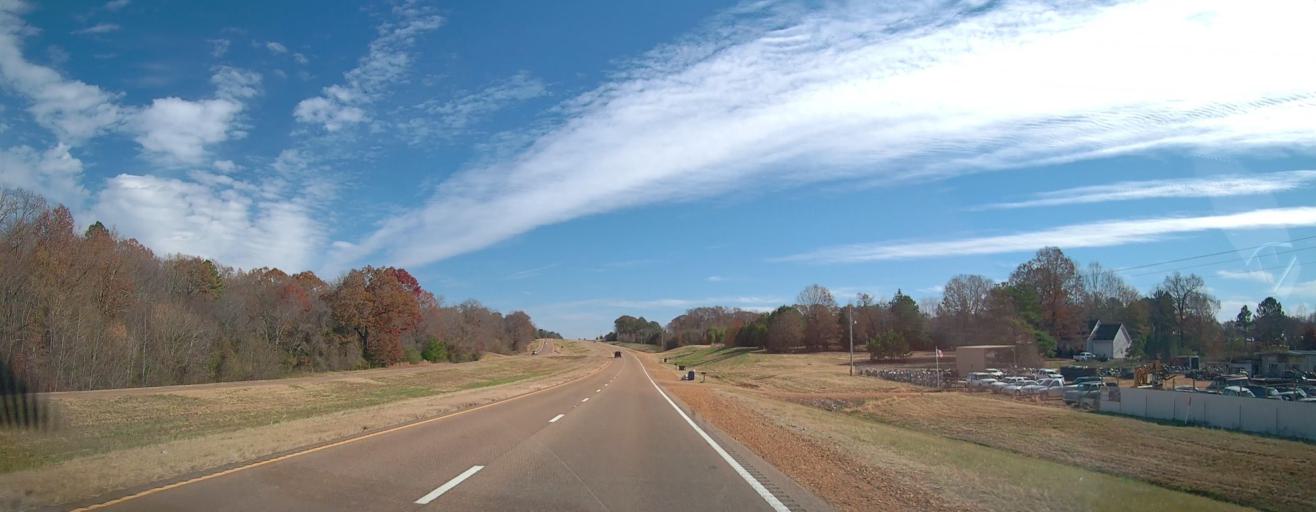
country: US
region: Mississippi
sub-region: Benton County
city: Ashland
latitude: 34.9458
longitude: -89.3347
